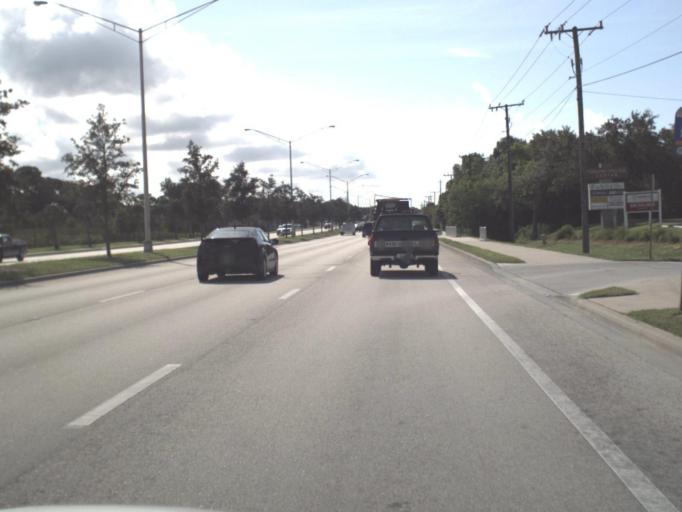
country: US
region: Florida
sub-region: Sarasota County
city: Laurel
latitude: 27.1373
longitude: -82.4576
